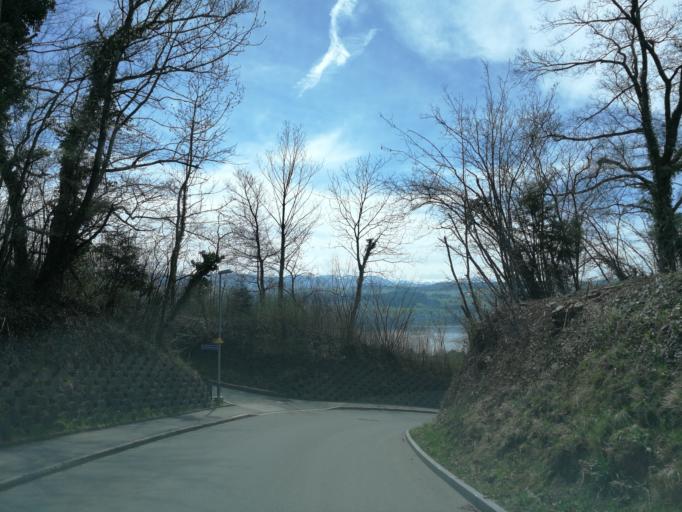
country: CH
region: Zurich
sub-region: Bezirk Meilen
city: Meilen
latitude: 47.2748
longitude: 8.6525
